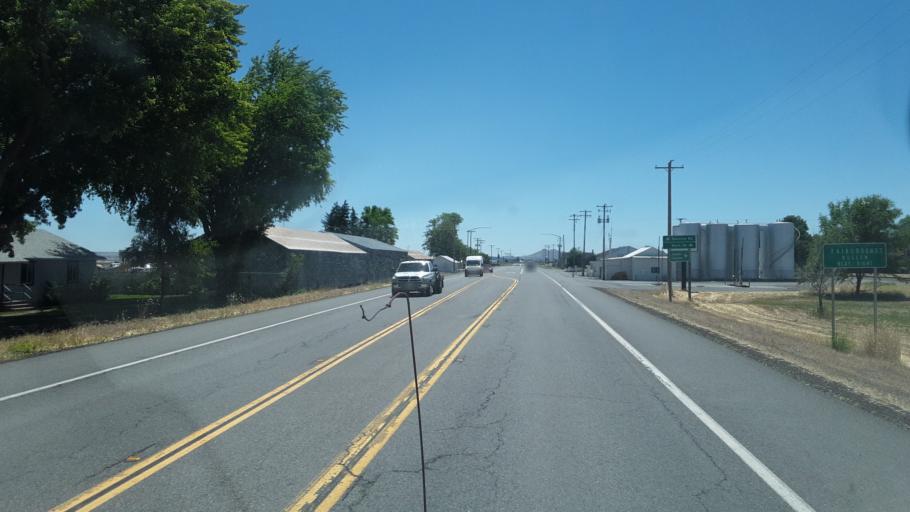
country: US
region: California
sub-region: Siskiyou County
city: Tulelake
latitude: 41.9600
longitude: -121.4767
